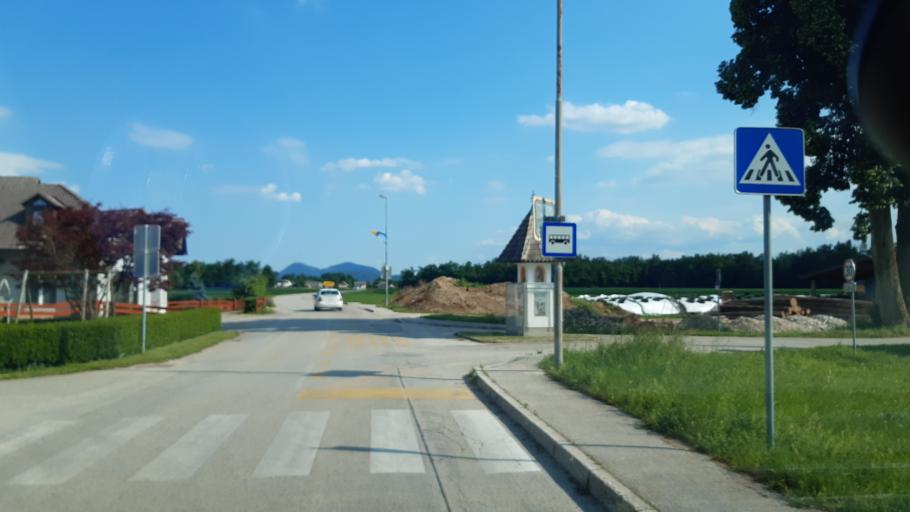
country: SI
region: Sencur
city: Hrastje
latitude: 46.2100
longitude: 14.3987
